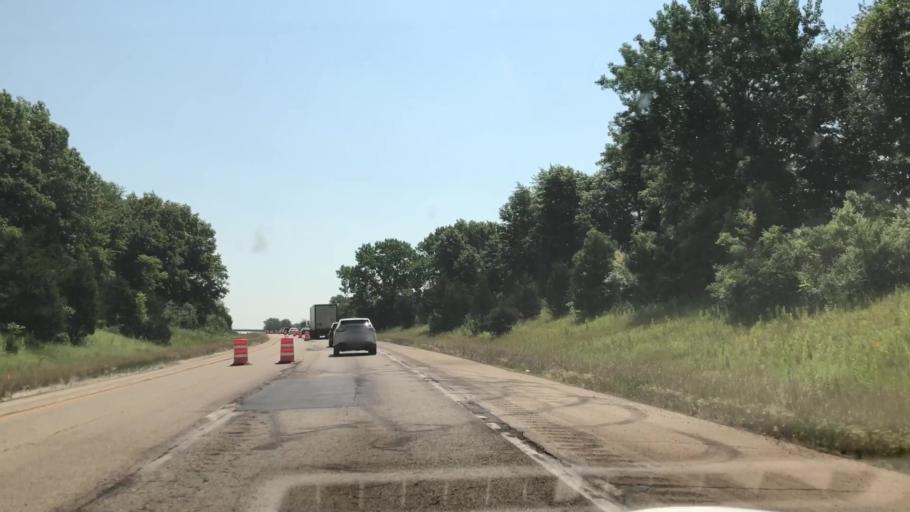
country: US
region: Illinois
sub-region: McLean County
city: Danvers
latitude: 40.6096
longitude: -89.2317
